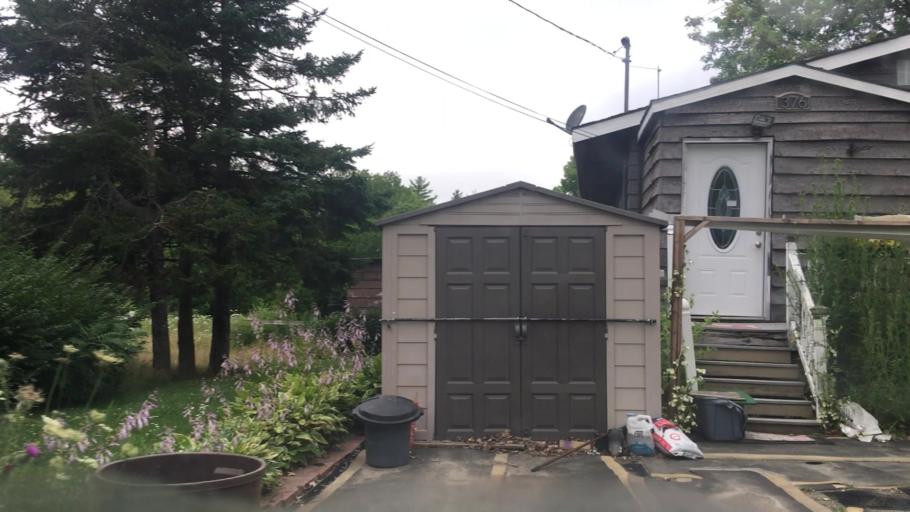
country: US
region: Maine
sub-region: Penobscot County
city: Veazie
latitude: 44.8526
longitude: -68.7440
